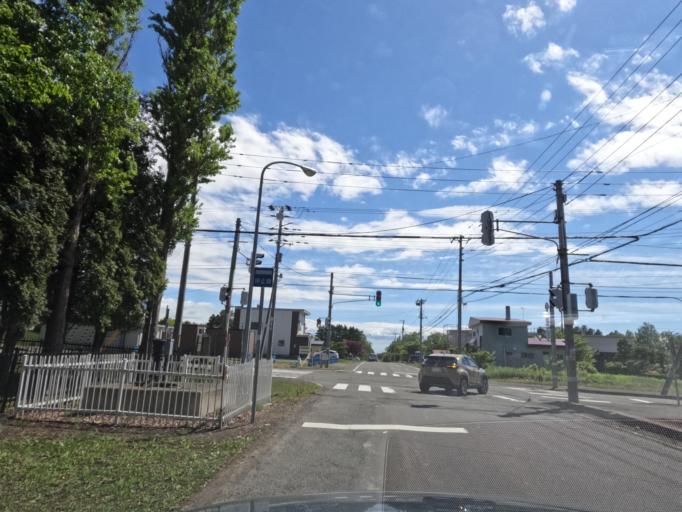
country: JP
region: Hokkaido
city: Kitahiroshima
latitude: 42.9991
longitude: 141.7236
